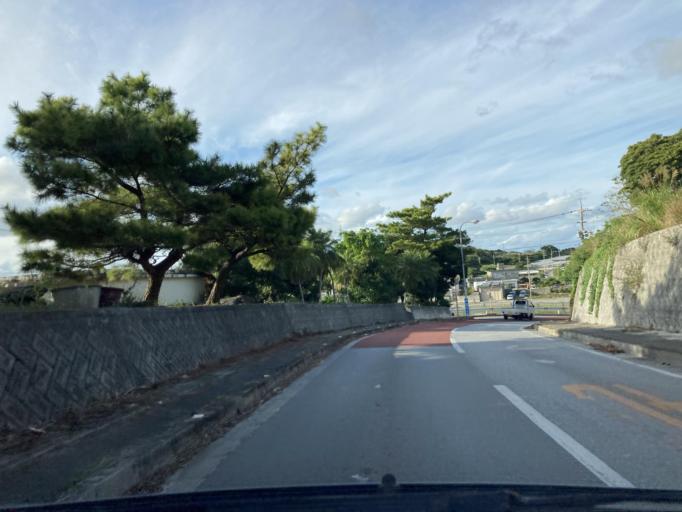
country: JP
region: Okinawa
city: Tomigusuku
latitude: 26.1588
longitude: 127.7373
